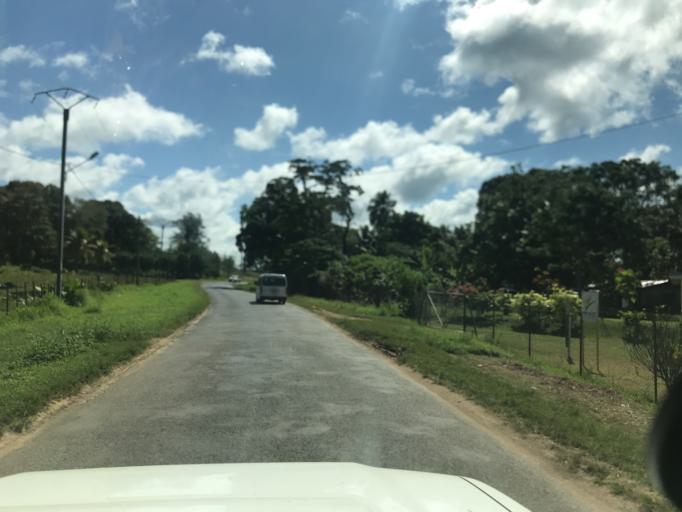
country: VU
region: Sanma
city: Luganville
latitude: -15.5276
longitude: 167.1546
